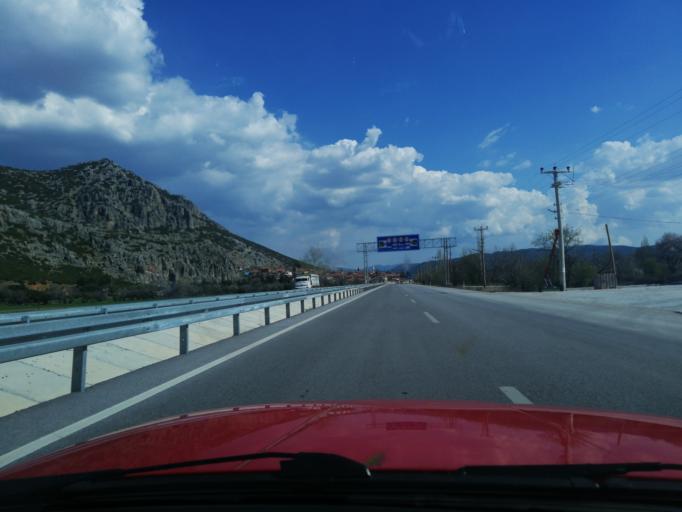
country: TR
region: Burdur
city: Celtikci
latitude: 37.5408
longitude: 30.4743
